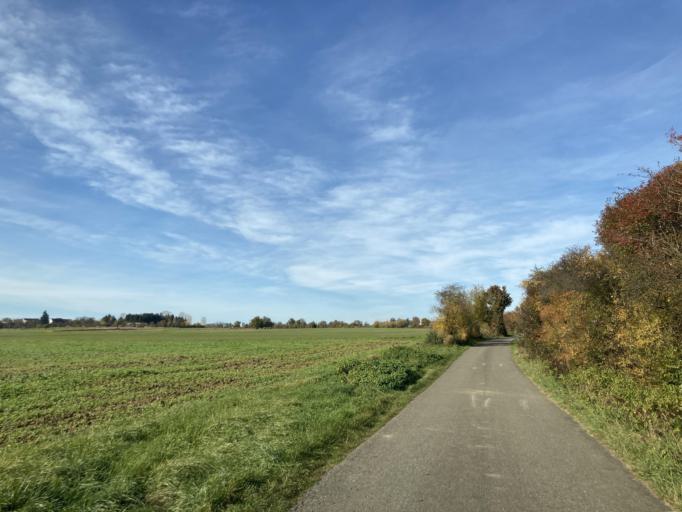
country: DE
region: Baden-Wuerttemberg
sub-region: Tuebingen Region
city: Bodelshausen
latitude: 48.3831
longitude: 8.9576
